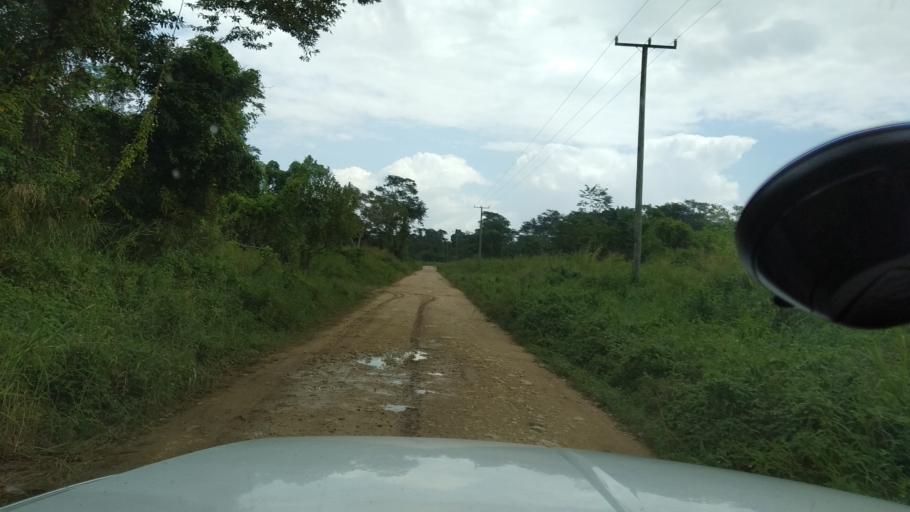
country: BZ
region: Toledo
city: Punta Gorda
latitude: 16.2203
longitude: -88.9955
